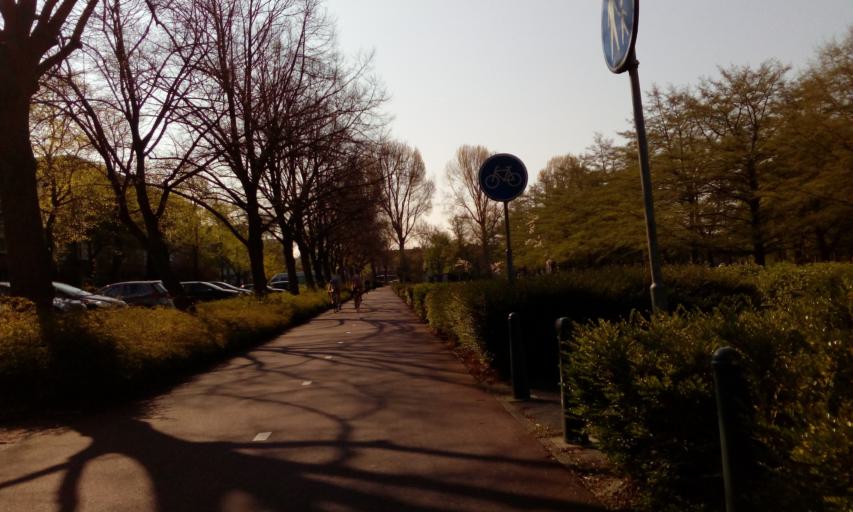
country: NL
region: South Holland
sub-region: Gemeente Rotterdam
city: Rotterdam
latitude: 51.9312
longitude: 4.4551
